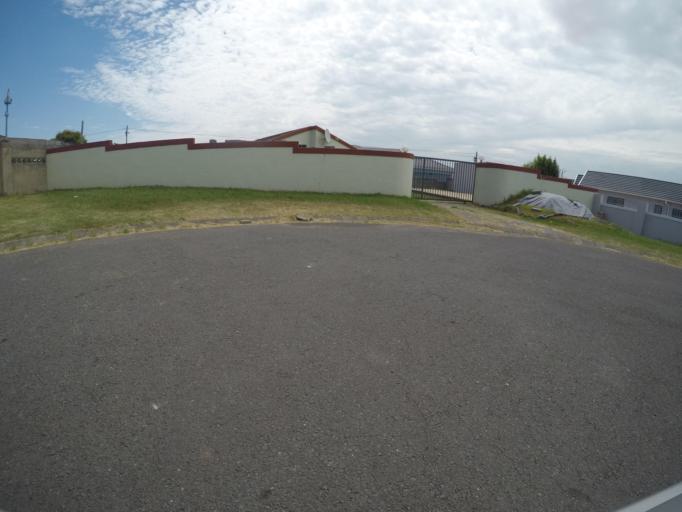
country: ZA
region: Eastern Cape
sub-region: Buffalo City Metropolitan Municipality
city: East London
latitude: -32.9912
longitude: 27.8667
